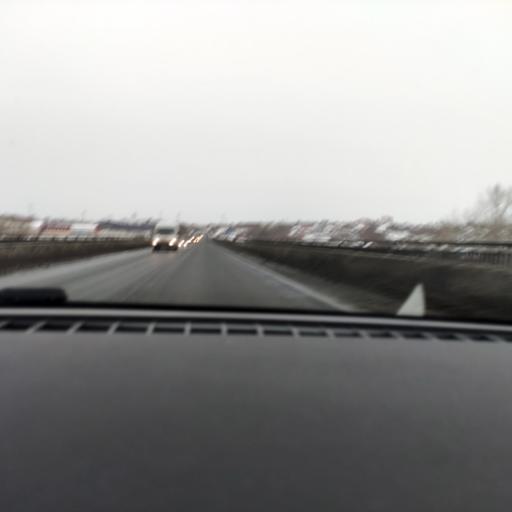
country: RU
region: Samara
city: Smyshlyayevka
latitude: 53.2323
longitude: 50.4895
